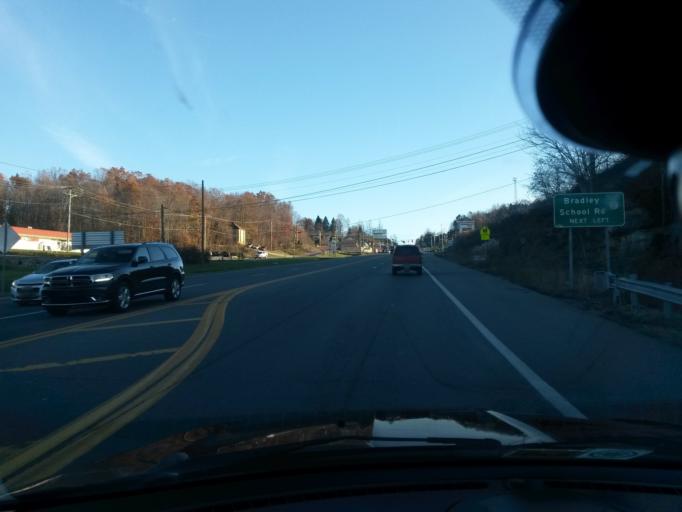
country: US
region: West Virginia
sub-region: Raleigh County
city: Prosperity
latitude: 37.8502
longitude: -81.1967
